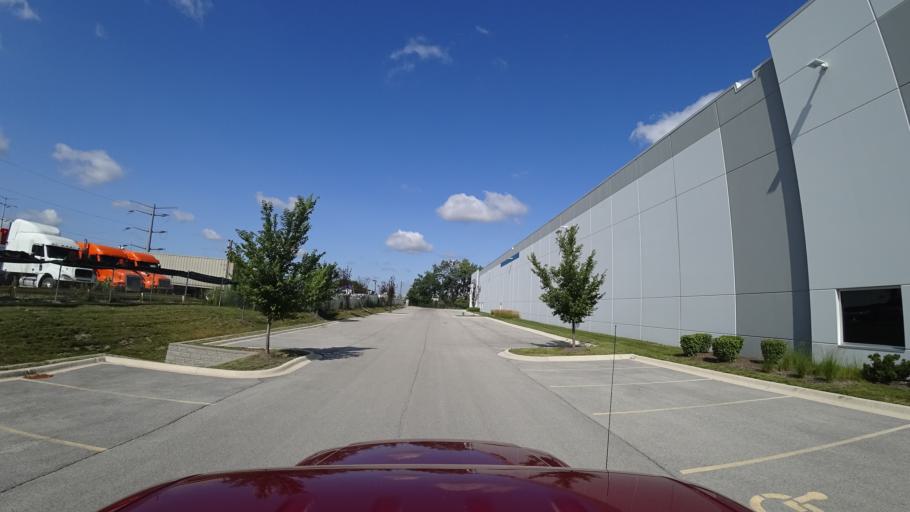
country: US
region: Illinois
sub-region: Cook County
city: Cicero
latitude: 41.8314
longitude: -87.7273
